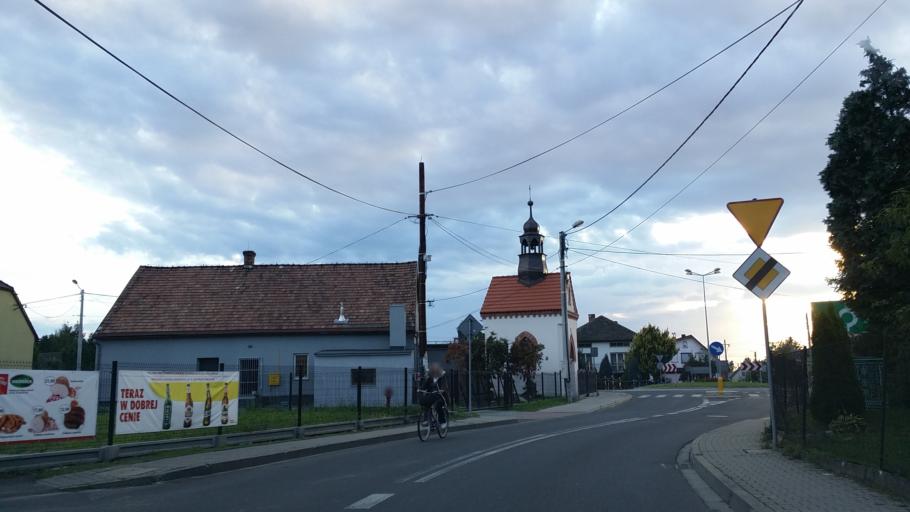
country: PL
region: Lesser Poland Voivodeship
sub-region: Powiat oswiecimski
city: Nowa Wies
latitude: 49.9066
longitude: 19.2176
